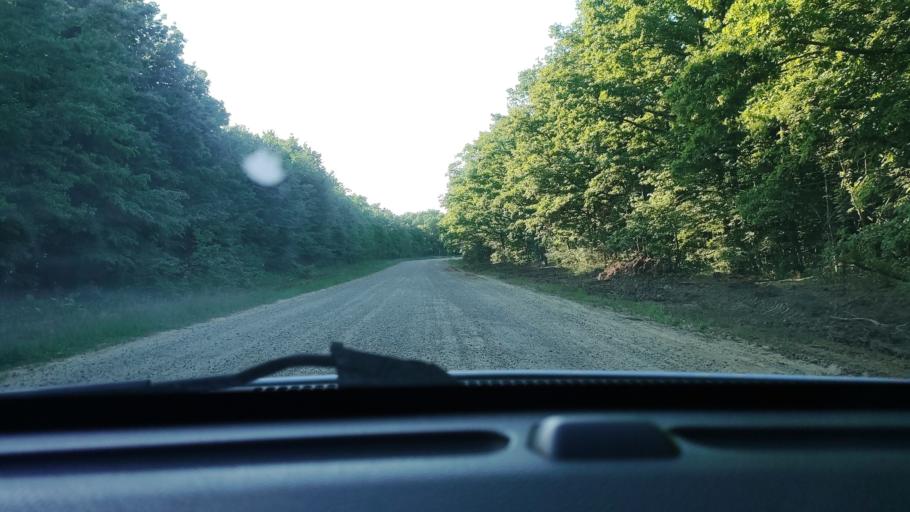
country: RU
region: Krasnodarskiy
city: Novodmitriyevskaya
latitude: 44.7190
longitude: 38.9912
